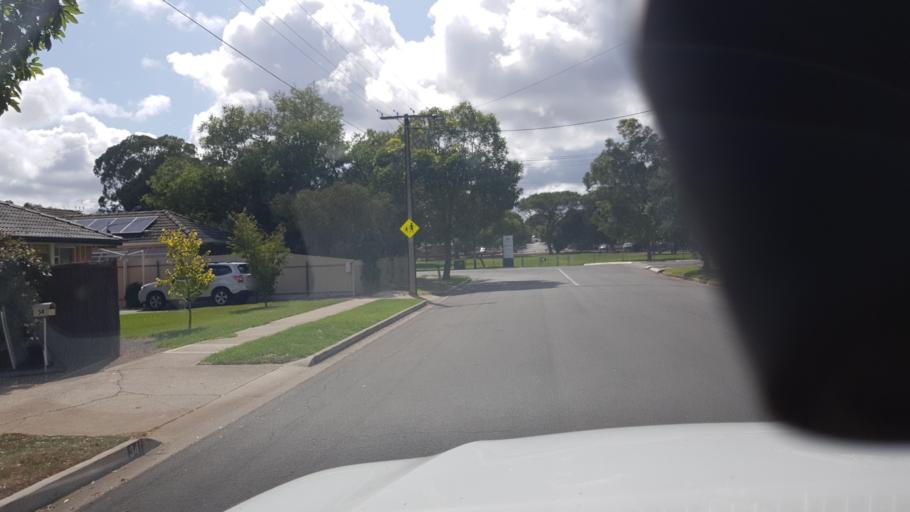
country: AU
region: South Australia
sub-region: Holdfast Bay
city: Seacliff Park
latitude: -35.0250
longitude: 138.5273
